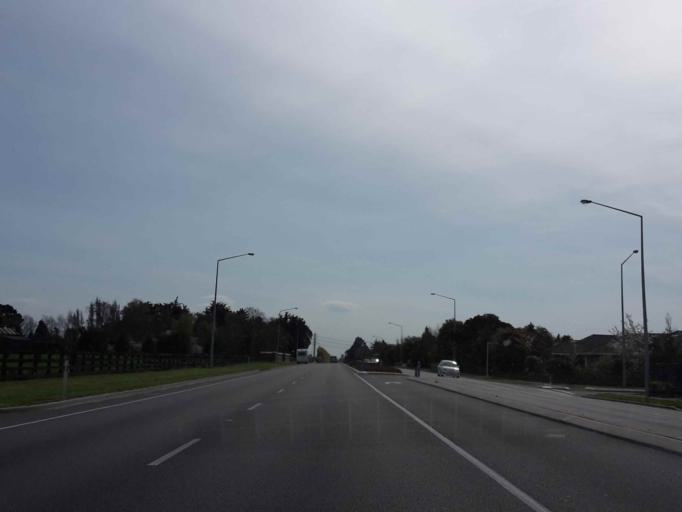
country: NZ
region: Canterbury
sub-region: Selwyn District
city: Prebbleton
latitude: -43.5178
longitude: 172.5355
